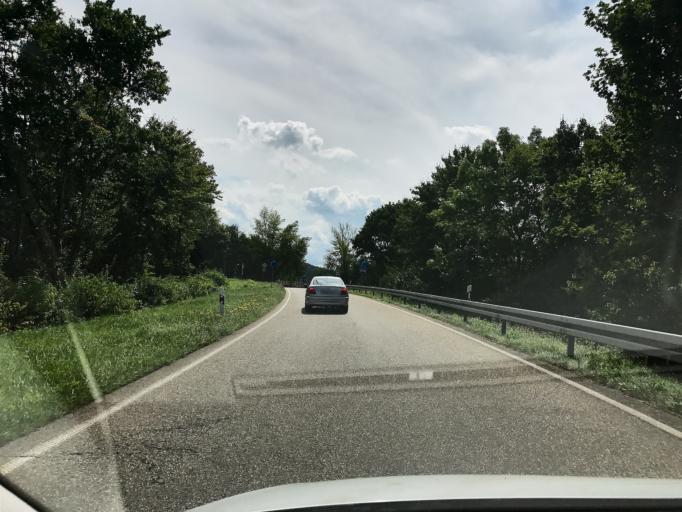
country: DE
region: Baden-Wuerttemberg
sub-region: Freiburg Region
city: Steinach
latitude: 48.2863
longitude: 8.0736
